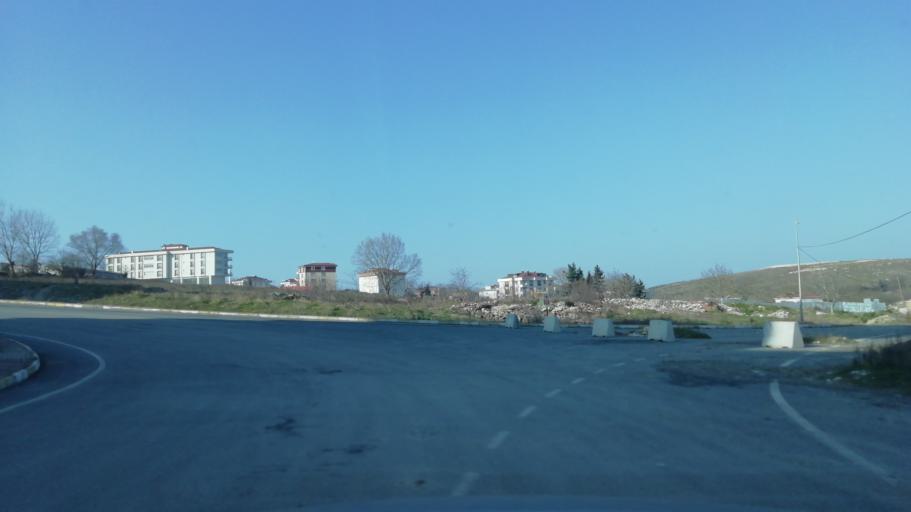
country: TR
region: Istanbul
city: Esenyurt
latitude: 41.1113
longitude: 28.6430
